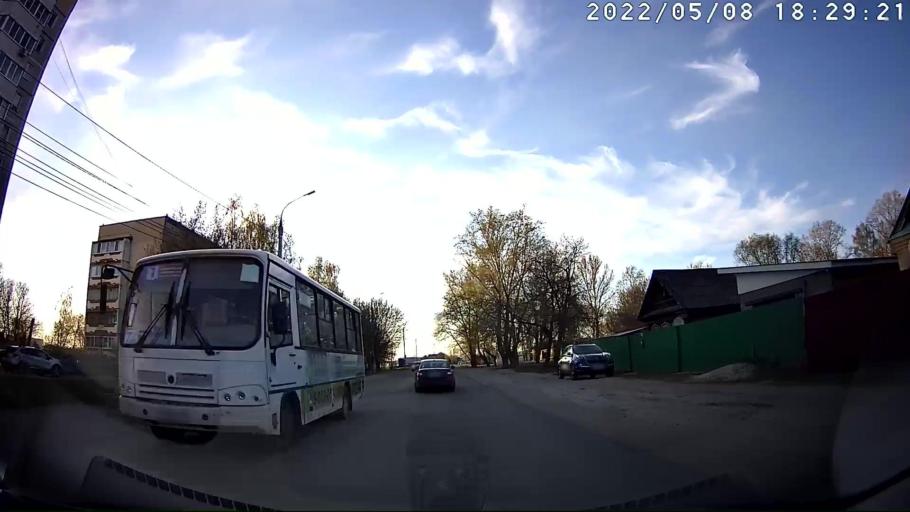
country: RU
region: Mariy-El
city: Volzhsk
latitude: 55.8670
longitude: 48.3712
